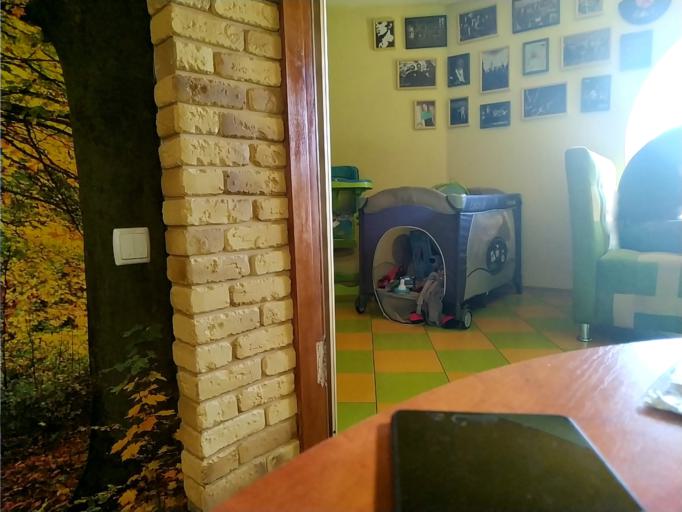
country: RU
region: Rjazan
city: Putyatino
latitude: 54.0708
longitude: 41.1738
